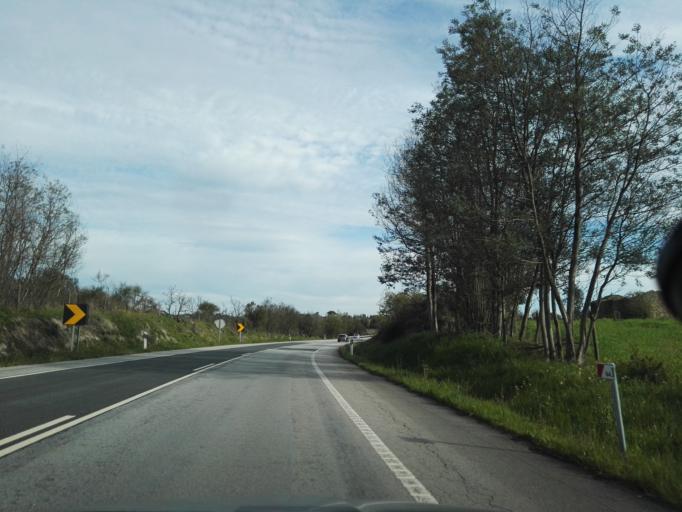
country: PT
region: Portalegre
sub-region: Nisa
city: Nisa
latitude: 39.4579
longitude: -7.7391
